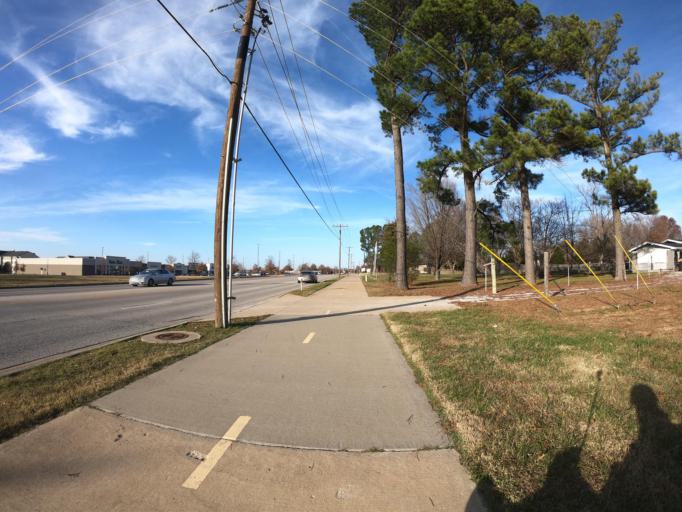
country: US
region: Arkansas
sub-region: Benton County
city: Bentonville
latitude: 36.3311
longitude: -94.1750
